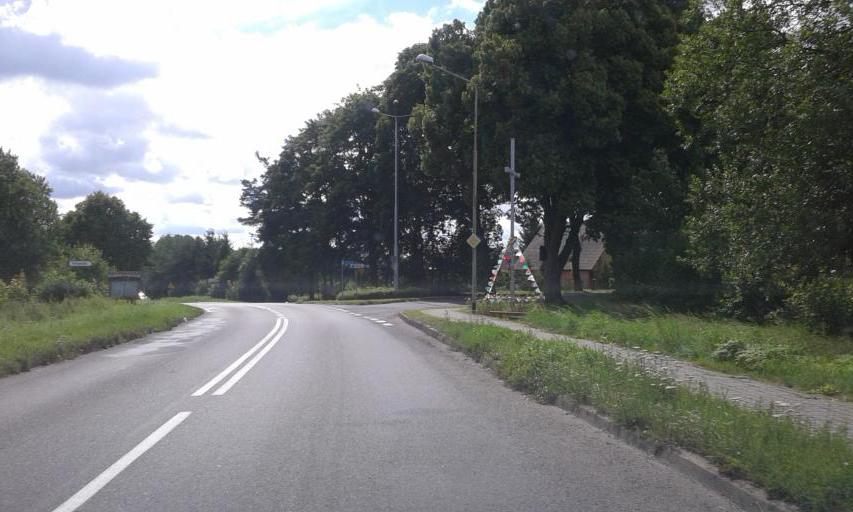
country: PL
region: West Pomeranian Voivodeship
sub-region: Powiat drawski
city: Czaplinek
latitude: 53.5468
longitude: 16.2447
